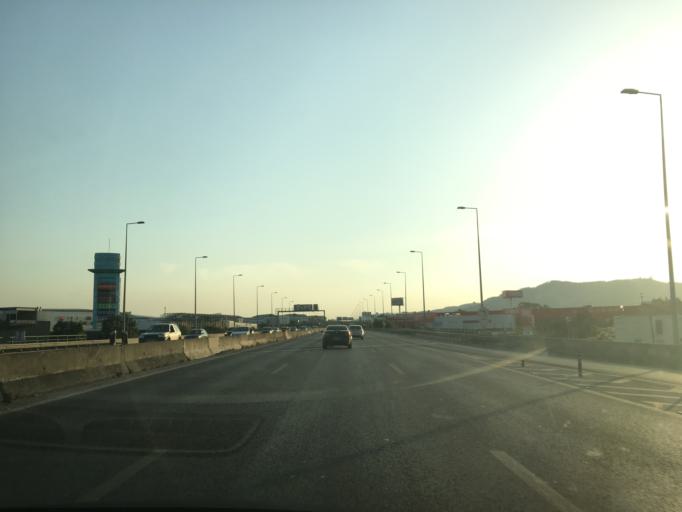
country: PT
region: Lisbon
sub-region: Sintra
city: Rio de Mouro
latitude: 38.7777
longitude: -9.3356
